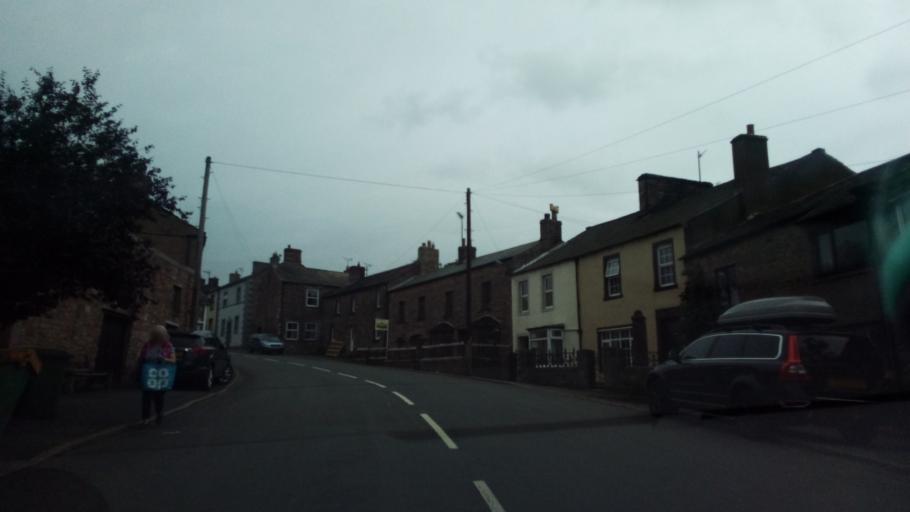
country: GB
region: England
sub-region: Cumbria
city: Kirkby Stephen
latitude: 54.5259
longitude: -2.3158
